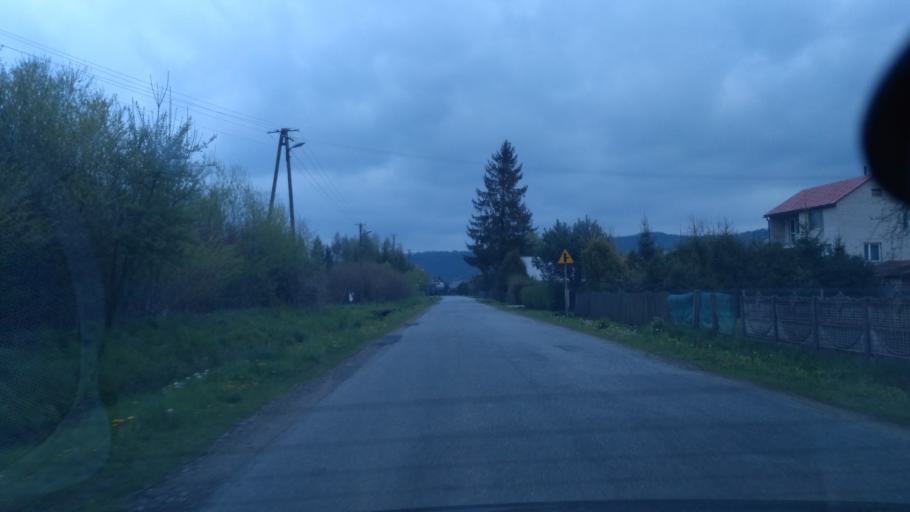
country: PL
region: Subcarpathian Voivodeship
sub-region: Powiat sanocki
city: Sanok
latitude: 49.6163
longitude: 22.2677
